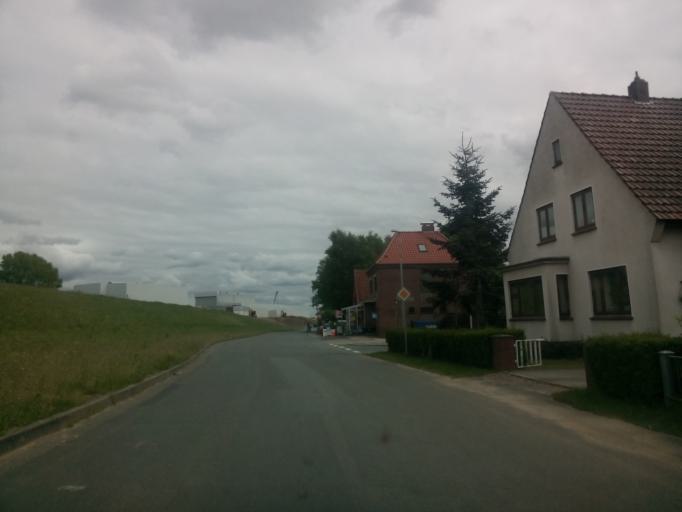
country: DE
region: Lower Saxony
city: Lemwerder
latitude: 53.1660
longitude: 8.6117
